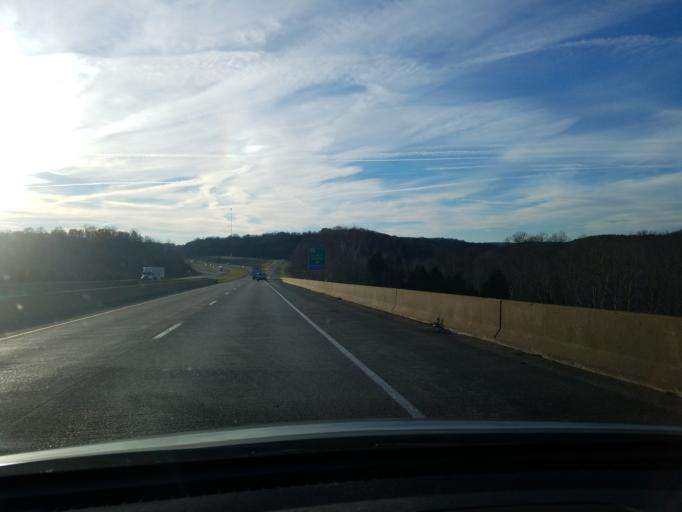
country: US
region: Indiana
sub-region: Crawford County
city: English
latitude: 38.2438
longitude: -86.4590
